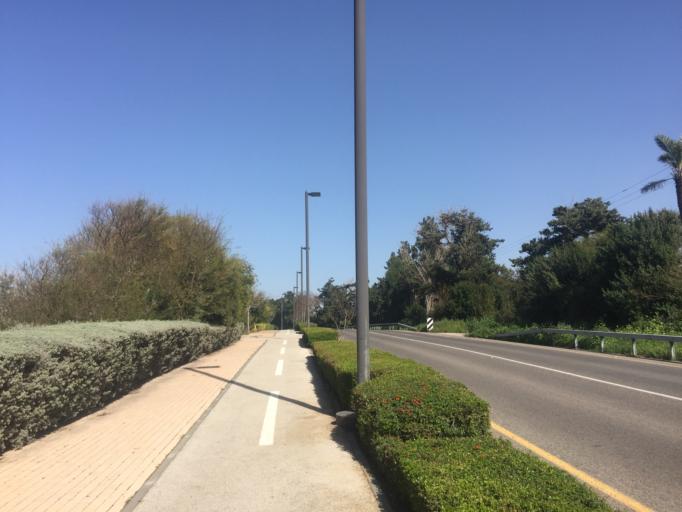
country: IL
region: Haifa
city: Qesarya
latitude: 32.5014
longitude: 34.9004
